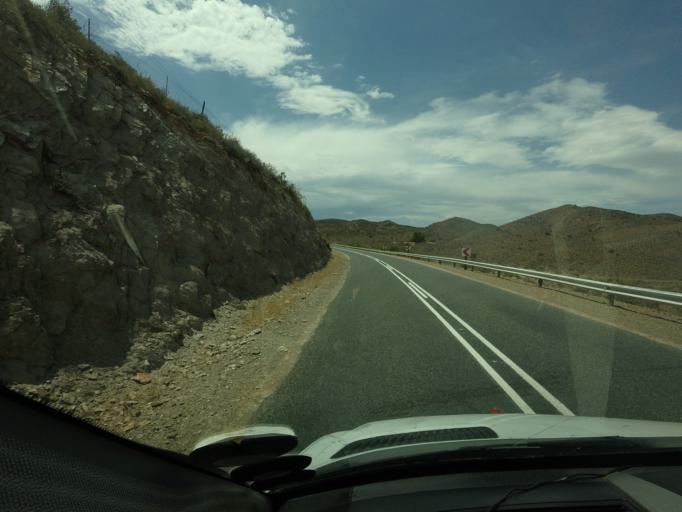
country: ZA
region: Western Cape
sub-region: Eden District Municipality
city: Ladismith
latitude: -33.7120
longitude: 20.9700
